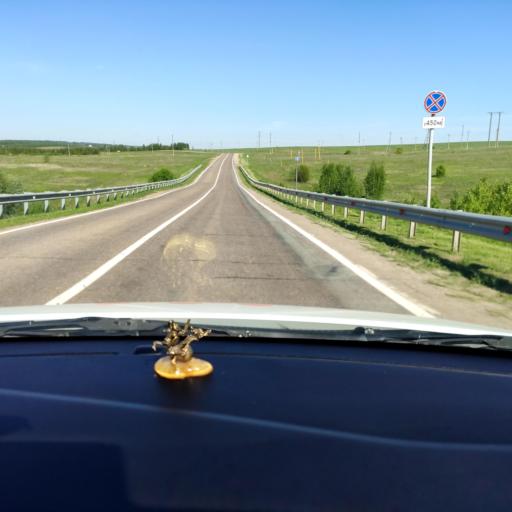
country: RU
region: Tatarstan
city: Vysokaya Gora
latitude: 56.0136
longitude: 49.2844
